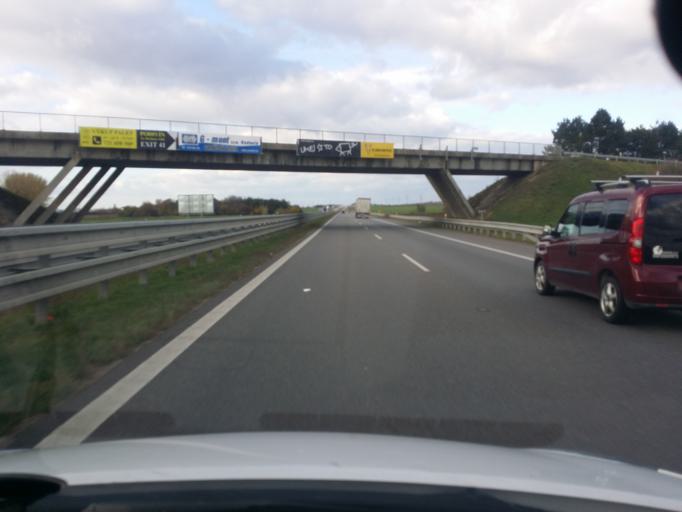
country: CZ
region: South Moravian
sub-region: Okres Breclav
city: Moravsky Zizkov
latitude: 48.7952
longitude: 16.9112
